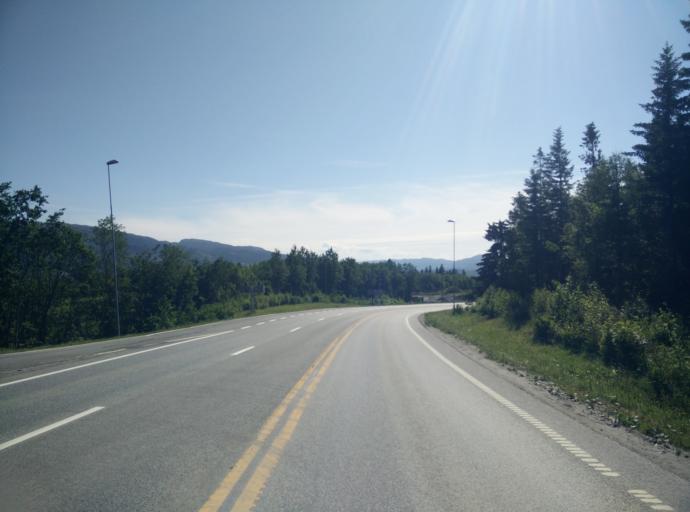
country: NO
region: Sor-Trondelag
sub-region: Melhus
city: Melhus
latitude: 63.3296
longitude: 10.3524
